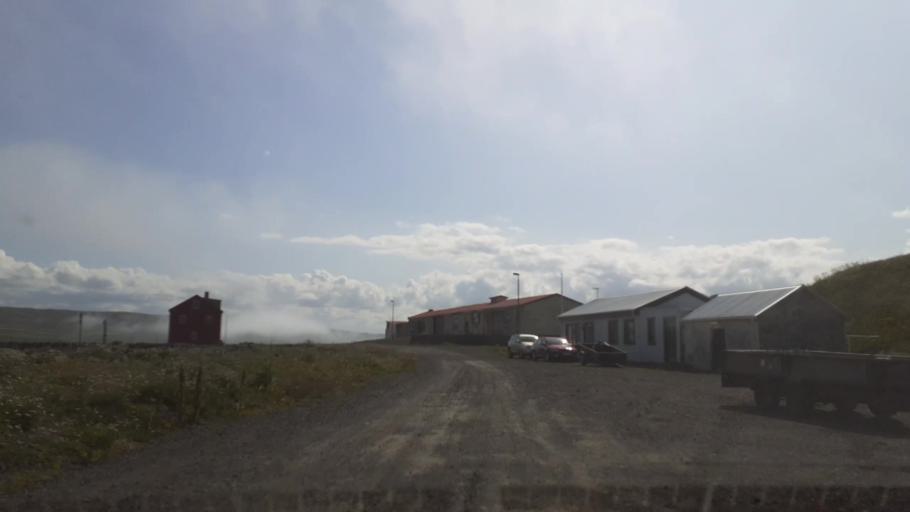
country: IS
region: West
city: Borgarnes
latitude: 65.2104
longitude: -21.0953
